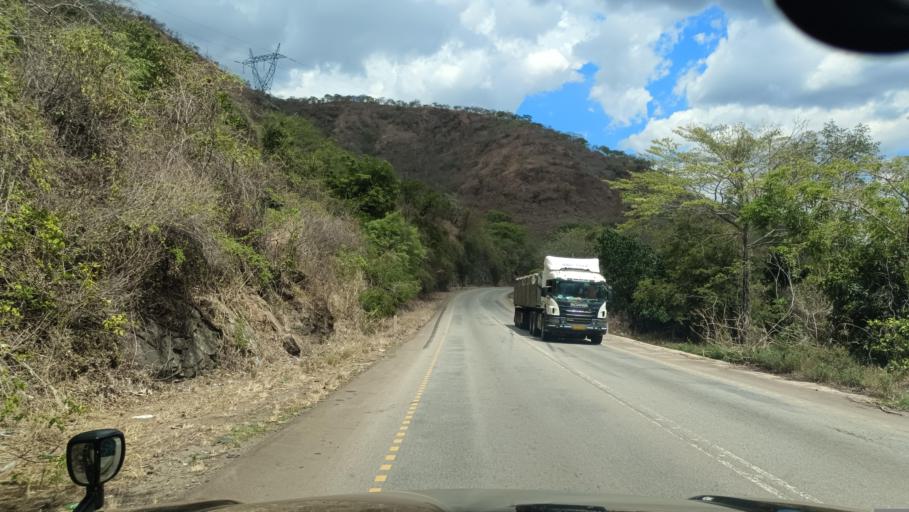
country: TZ
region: Morogoro
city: Kidatu
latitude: -7.5756
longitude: 36.7530
